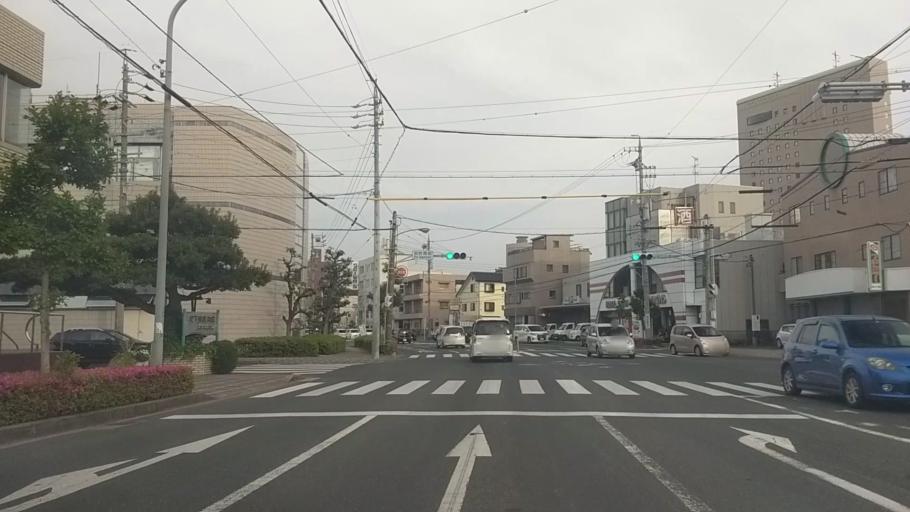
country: JP
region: Shizuoka
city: Hamamatsu
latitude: 34.7159
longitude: 137.7259
